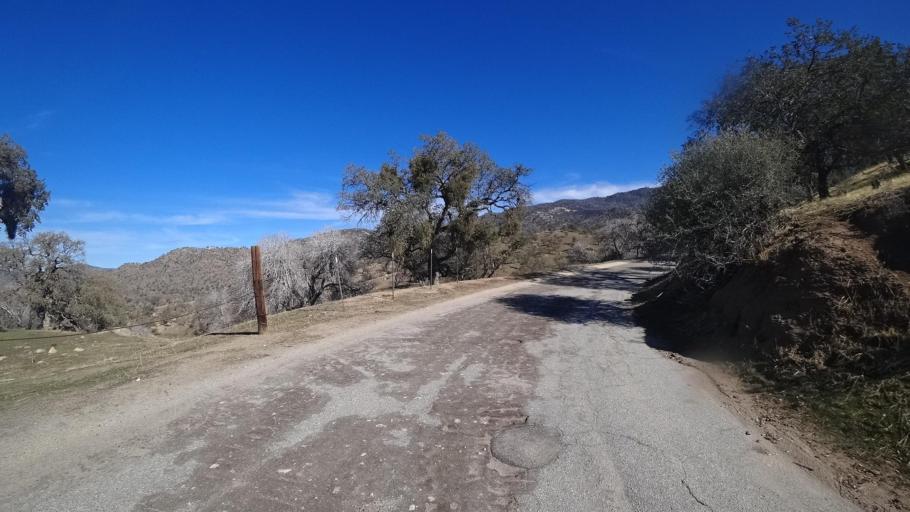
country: US
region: California
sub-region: Kern County
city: Bodfish
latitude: 35.4438
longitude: -118.6830
